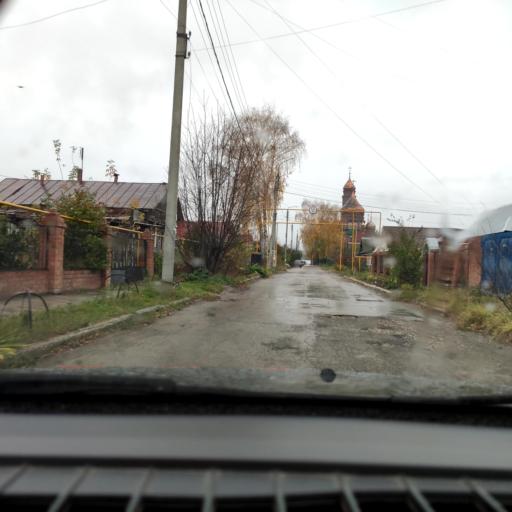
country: RU
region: Samara
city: Tol'yatti
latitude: 53.5281
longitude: 49.4103
